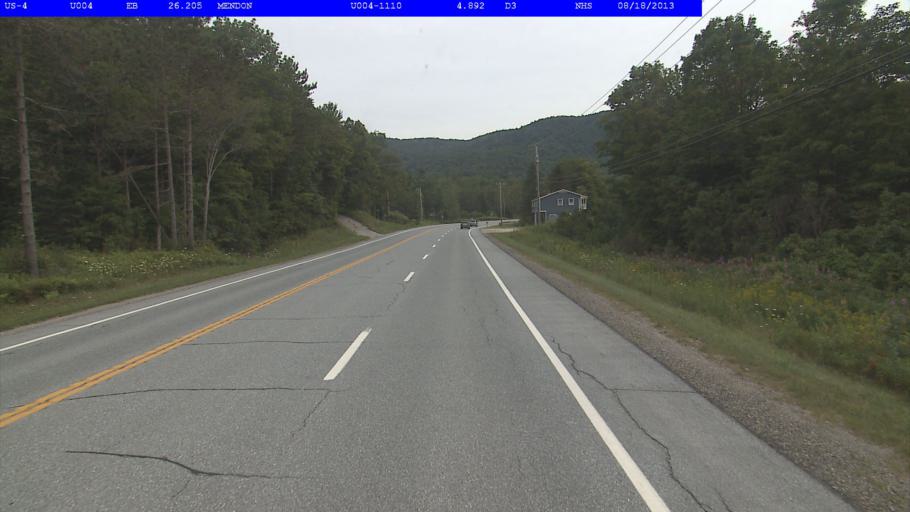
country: US
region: Vermont
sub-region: Rutland County
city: Rutland
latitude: 43.6637
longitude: -72.8642
